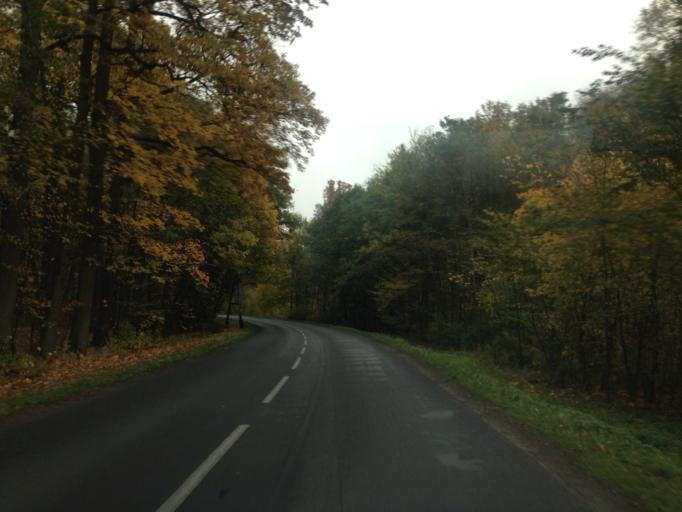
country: PL
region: Kujawsko-Pomorskie
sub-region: Powiat brodnicki
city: Bobrowo
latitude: 53.2688
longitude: 19.3198
